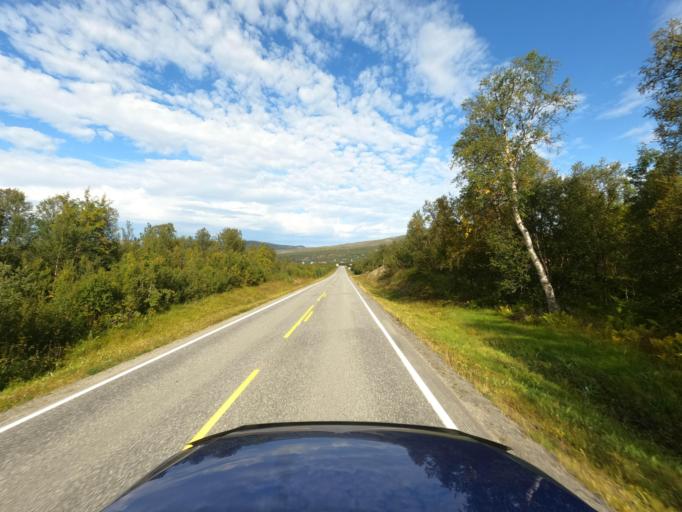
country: NO
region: Finnmark Fylke
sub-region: Kvalsund
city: Kvalsund
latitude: 70.4169
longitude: 24.5014
